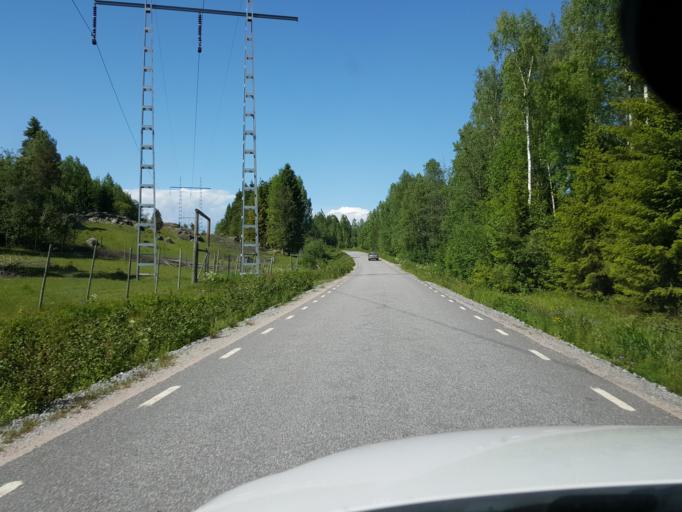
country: SE
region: Gaevleborg
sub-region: Ljusdals Kommun
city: Jaervsoe
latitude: 61.7285
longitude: 16.2858
